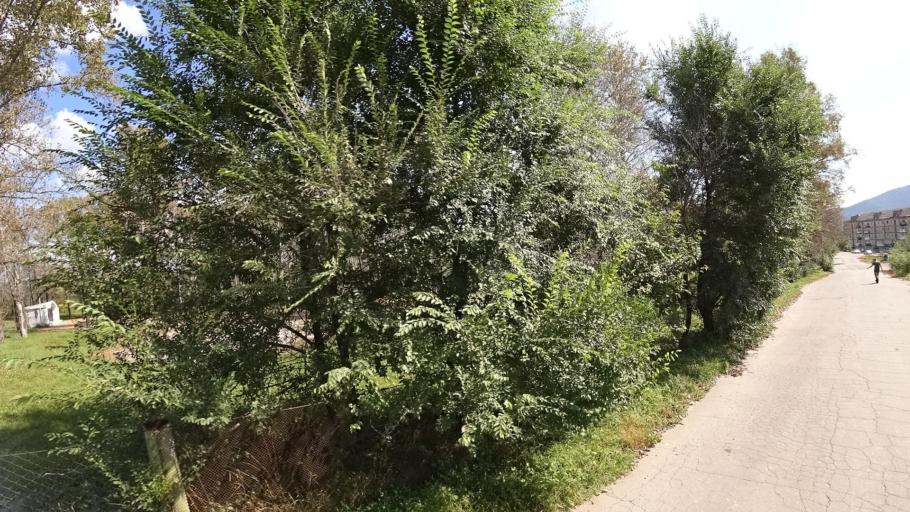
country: RU
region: Jewish Autonomous Oblast
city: Londoko
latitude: 49.0168
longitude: 131.8872
